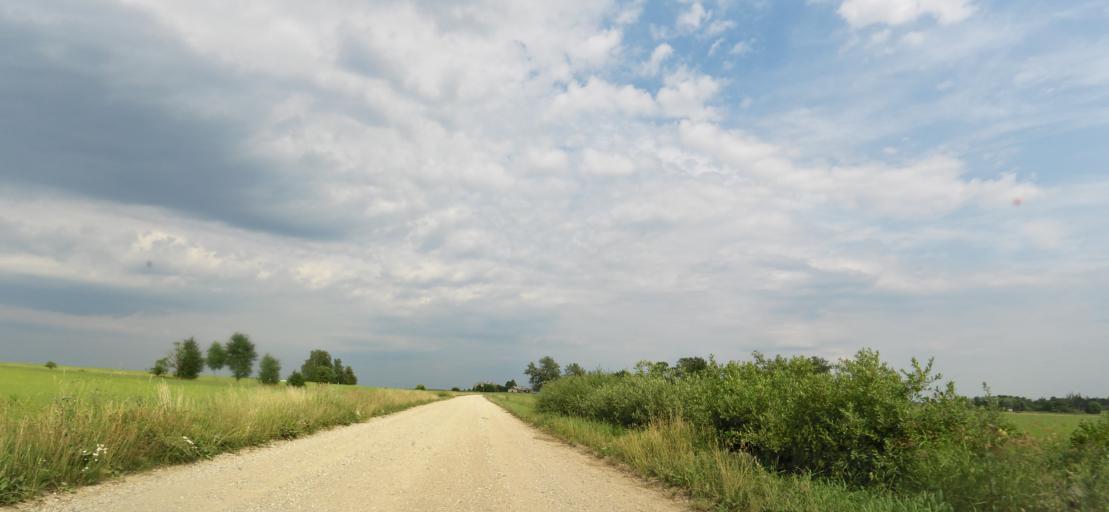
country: LT
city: Obeliai
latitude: 56.1526
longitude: 25.0307
